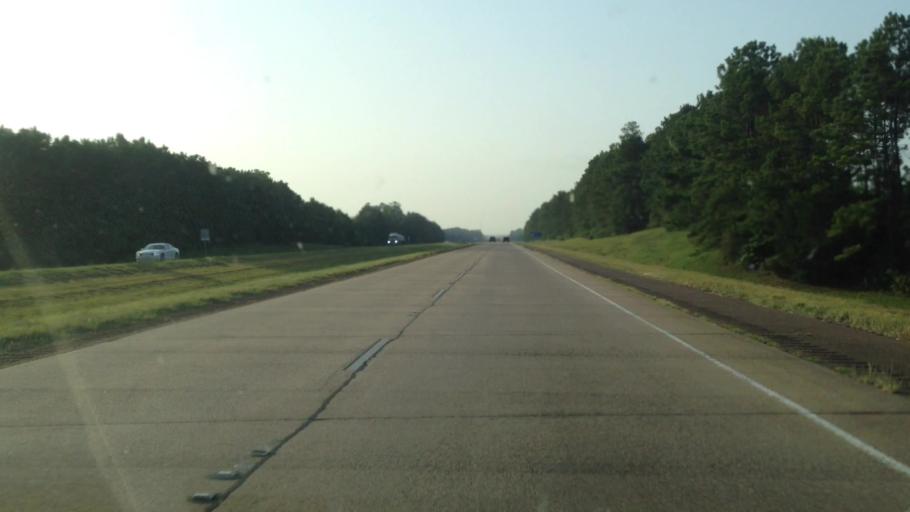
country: US
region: Louisiana
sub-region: Rapides Parish
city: Boyce
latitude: 31.4171
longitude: -92.7279
